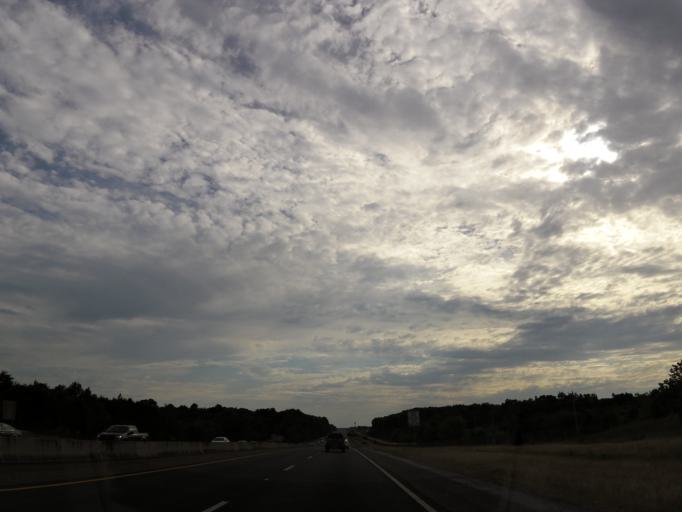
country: US
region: Alabama
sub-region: Madison County
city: Madison
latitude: 34.6522
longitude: -86.8147
